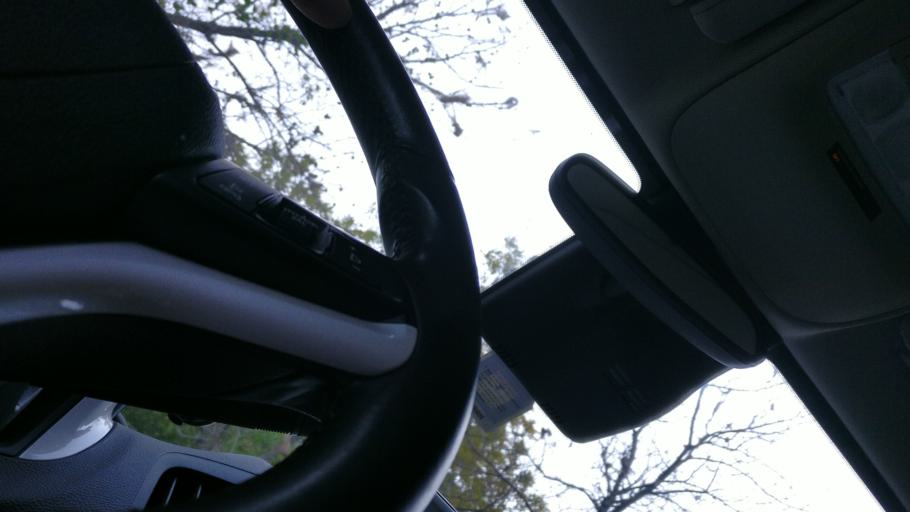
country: US
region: Oklahoma
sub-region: McClain County
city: Goldsby
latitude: 35.1896
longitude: -97.5320
